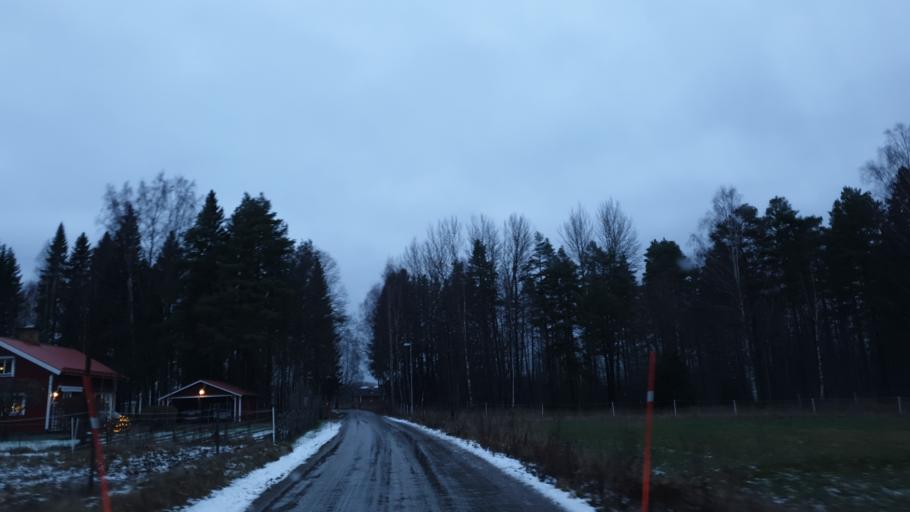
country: SE
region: Uppsala
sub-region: Tierps Kommun
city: Tierp
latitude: 60.3401
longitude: 17.4749
